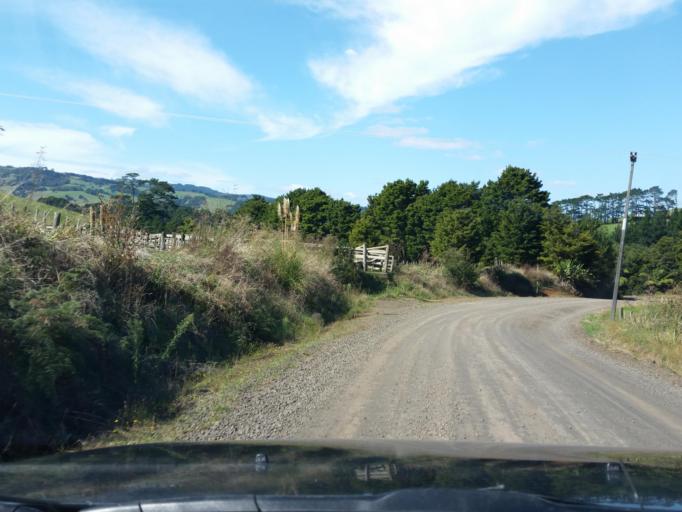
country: NZ
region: Northland
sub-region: Kaipara District
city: Dargaville
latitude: -35.7073
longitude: 173.5933
